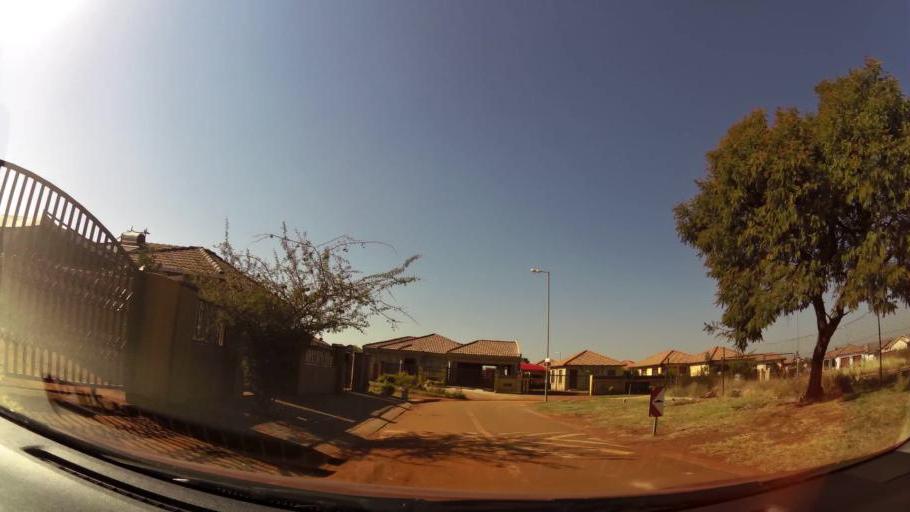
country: ZA
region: North-West
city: Ga-Rankuwa
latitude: -25.6358
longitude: 28.0783
